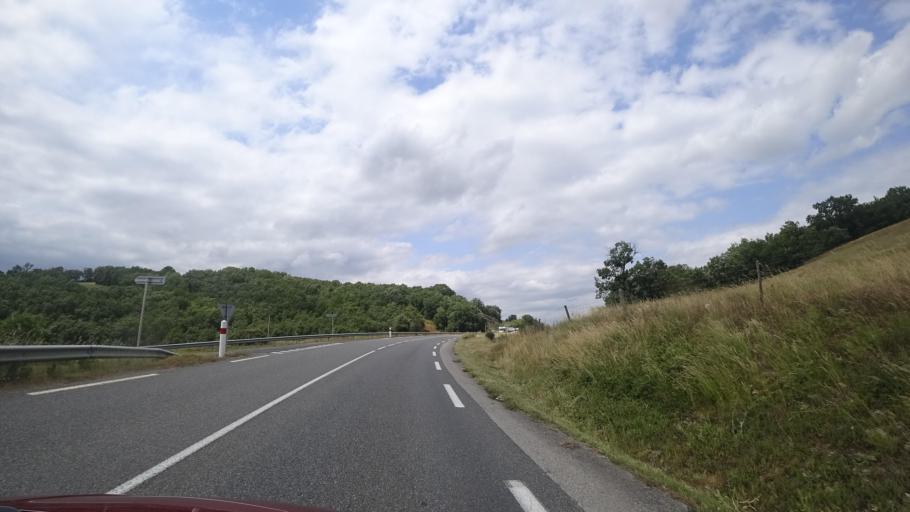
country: FR
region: Midi-Pyrenees
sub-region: Departement de l'Aveyron
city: Saint-Affrique
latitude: 43.9923
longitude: 2.9313
